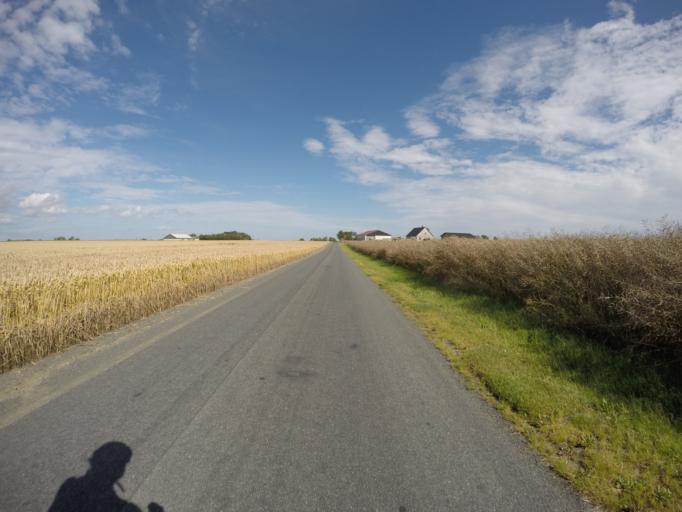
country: SE
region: Skane
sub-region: Simrishamns Kommun
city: Simrishamn
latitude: 55.4878
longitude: 14.1833
